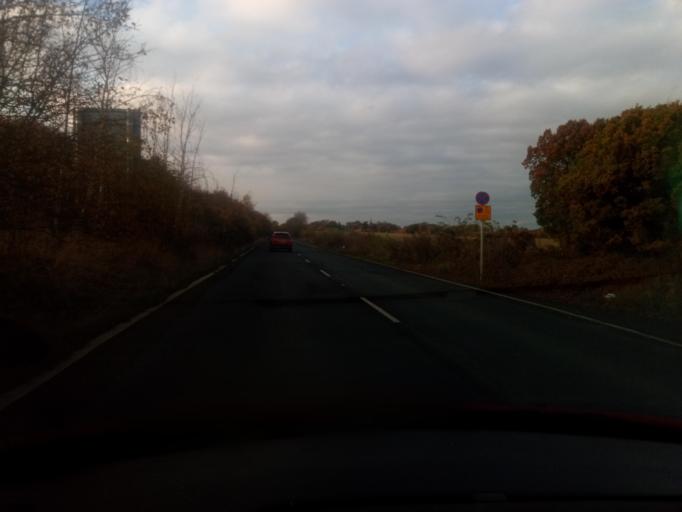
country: GB
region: England
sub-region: City and Borough of Leeds
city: Wetherby
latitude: 53.9397
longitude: -1.3806
